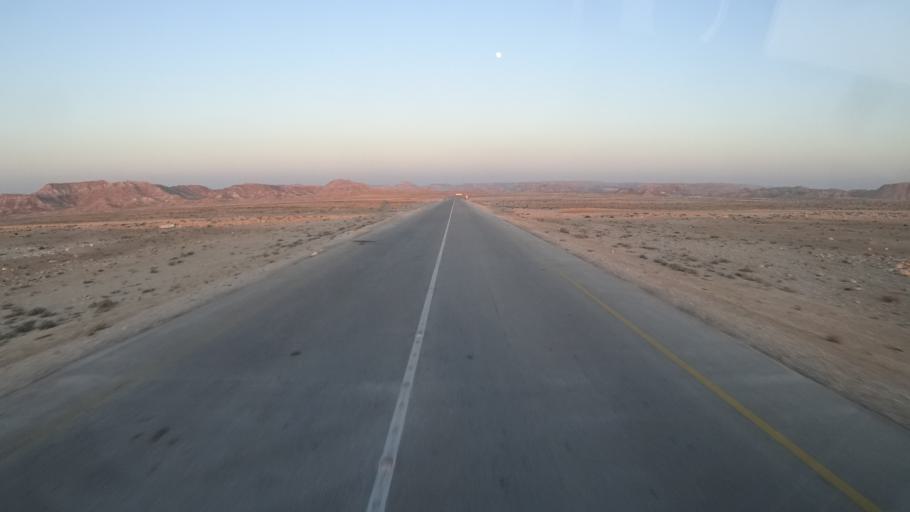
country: YE
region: Al Mahrah
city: Hawf
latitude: 16.9386
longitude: 53.3713
